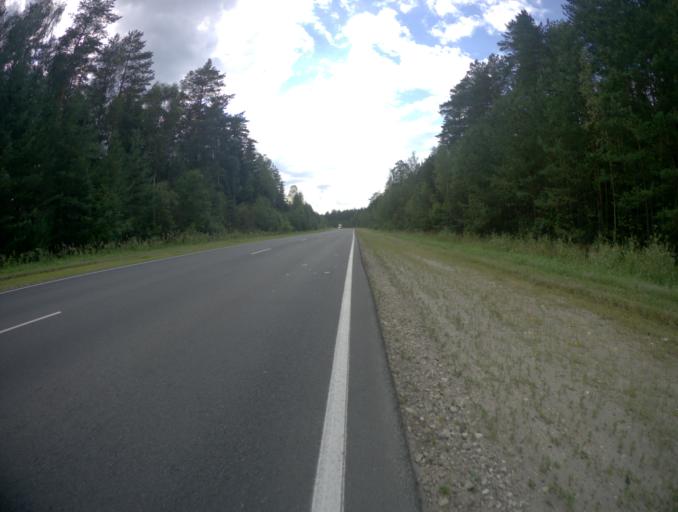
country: RU
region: Vladimir
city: Andreyevo
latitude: 55.9465
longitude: 41.0402
